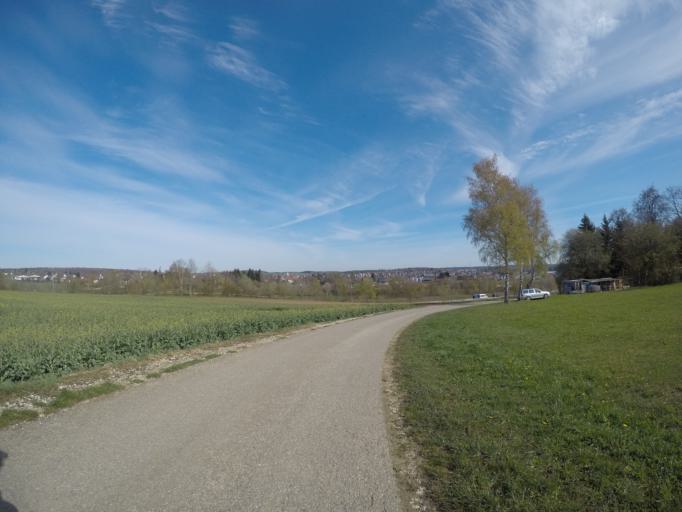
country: DE
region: Baden-Wuerttemberg
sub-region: Tuebingen Region
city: Laichingen
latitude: 48.4817
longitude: 9.6931
